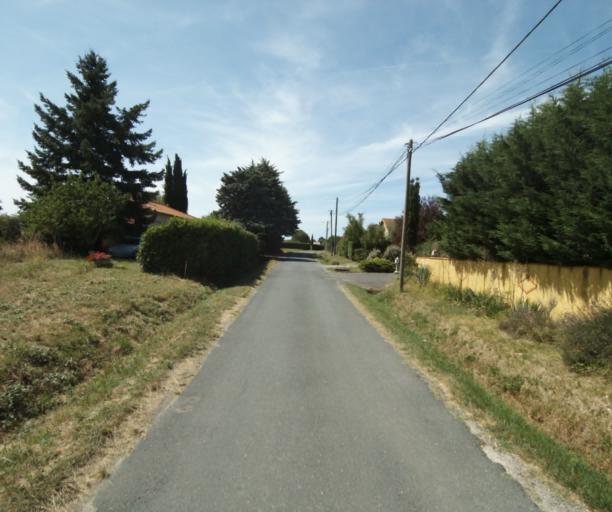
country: FR
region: Midi-Pyrenees
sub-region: Departement du Tarn
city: Puylaurens
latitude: 43.5337
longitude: 2.0164
